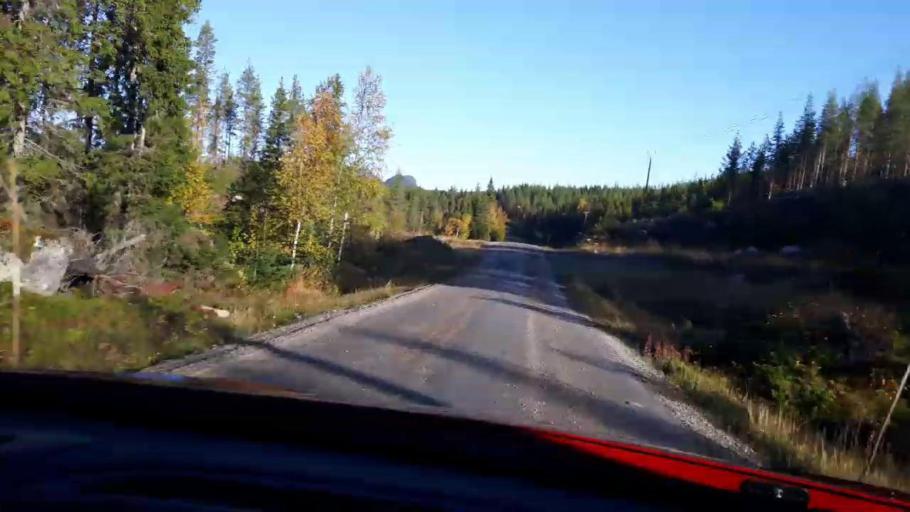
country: SE
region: Jaemtland
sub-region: Stroemsunds Kommun
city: Stroemsund
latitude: 64.3699
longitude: 15.1578
